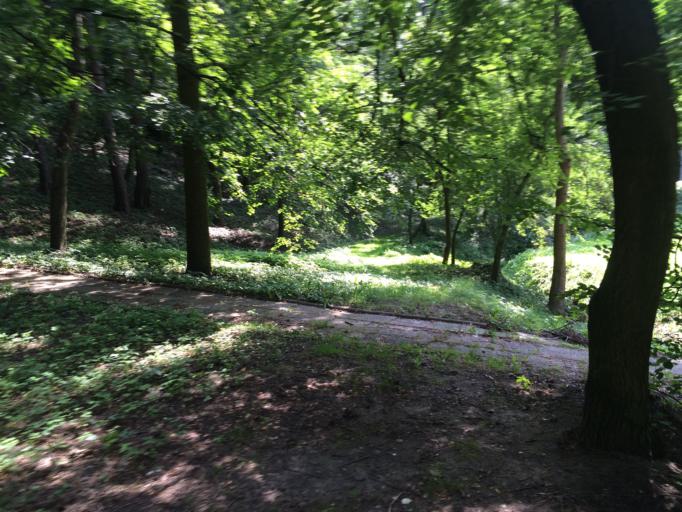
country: PL
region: Swietokrzyskie
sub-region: Powiat starachowicki
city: Starachowice
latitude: 51.0534
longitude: 21.0664
